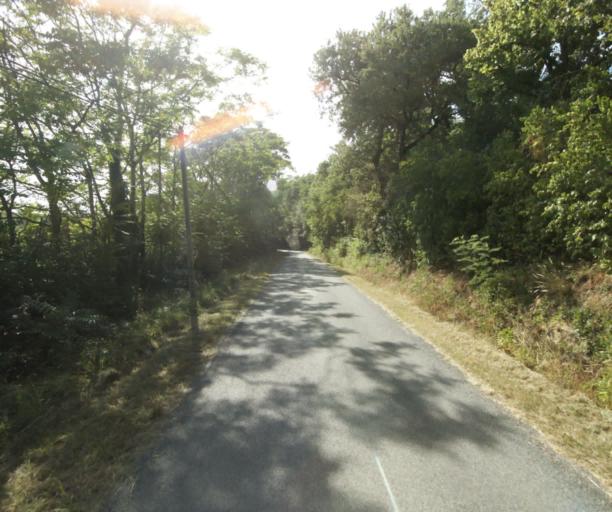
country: FR
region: Midi-Pyrenees
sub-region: Departement du Tarn
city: Soual
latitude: 43.5287
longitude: 2.0717
